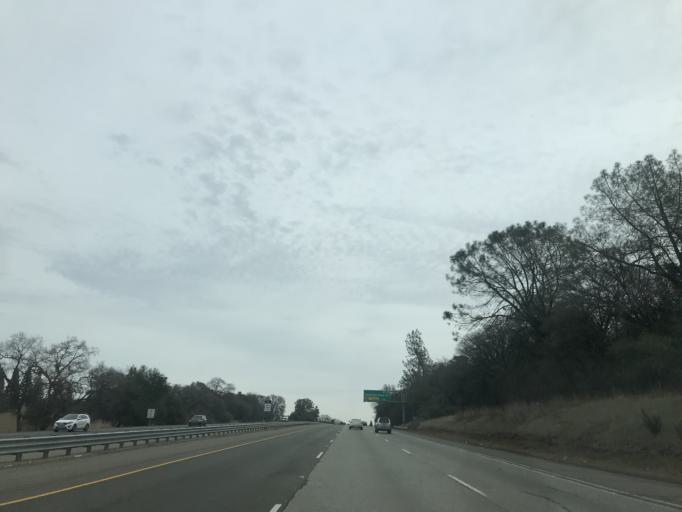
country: US
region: California
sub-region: El Dorado County
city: Cameron Park
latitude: 38.6577
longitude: -120.9836
